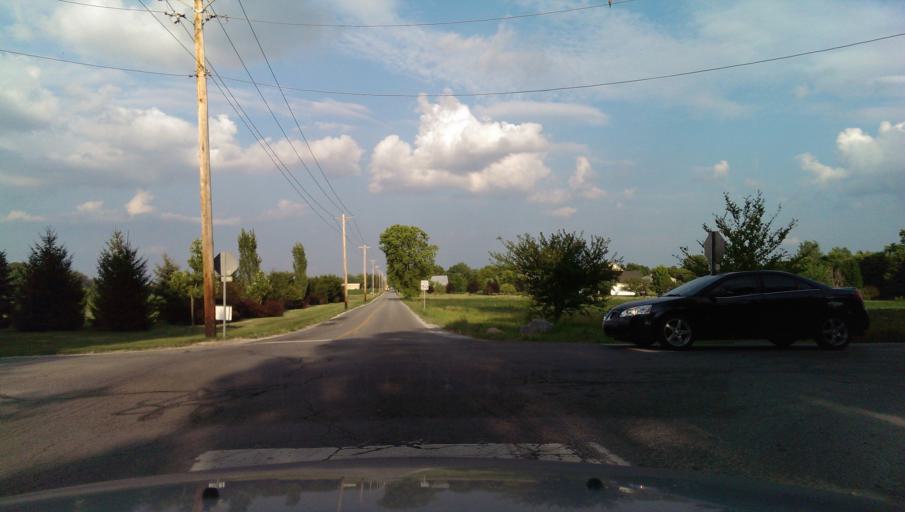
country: US
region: Indiana
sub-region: Hamilton County
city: Westfield
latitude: 40.0649
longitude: -86.1094
